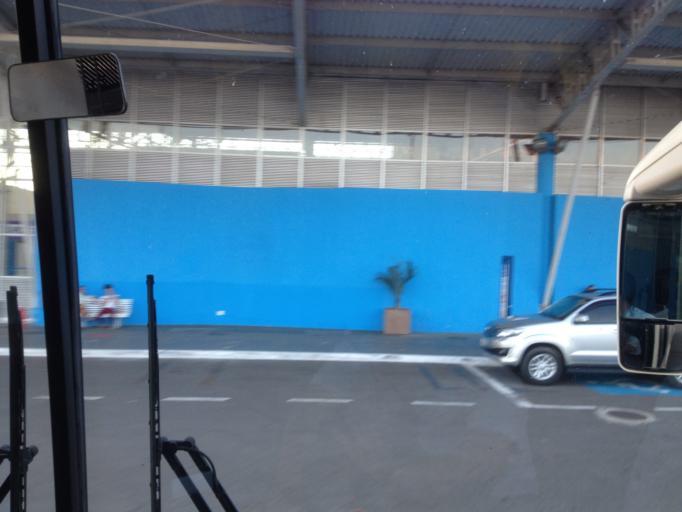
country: BR
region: Minas Gerais
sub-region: Rio Novo
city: Rio Novo
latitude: -21.5106
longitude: -43.1620
